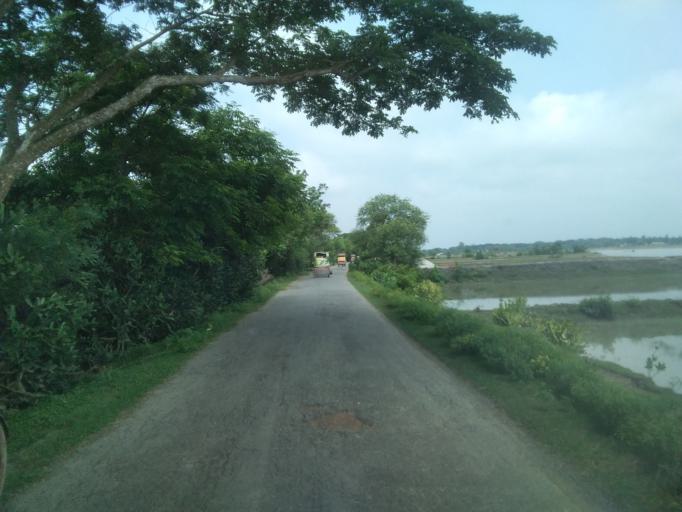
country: BD
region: Khulna
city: Phultala
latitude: 22.7048
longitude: 89.4648
